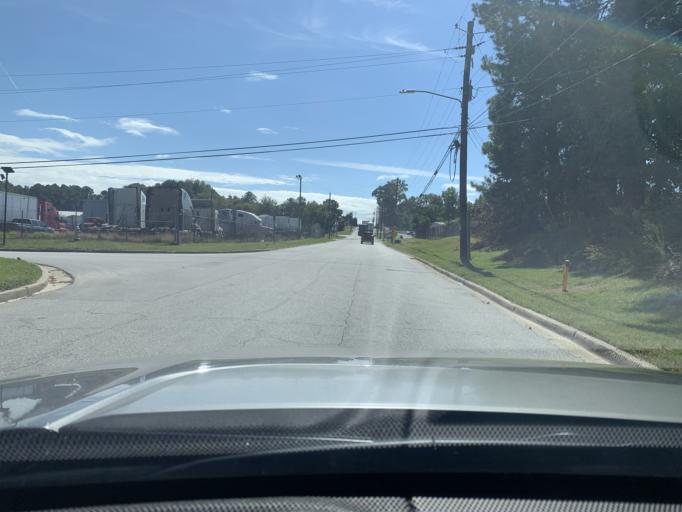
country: US
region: Georgia
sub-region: Clayton County
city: Conley
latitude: 33.6636
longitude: -84.3278
